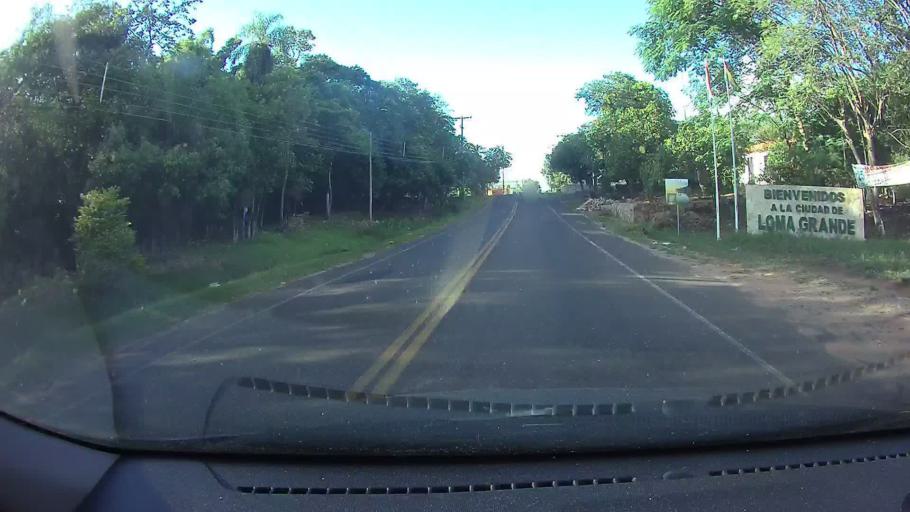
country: PY
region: Cordillera
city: Altos
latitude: -25.1810
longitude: -57.2310
